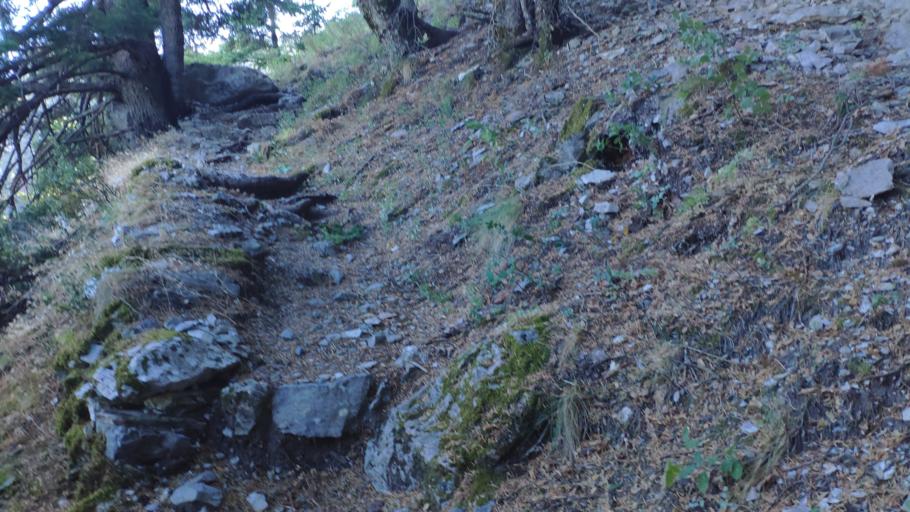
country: GR
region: Peloponnese
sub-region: Nomos Lakonias
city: Kariai
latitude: 37.1732
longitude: 22.6022
